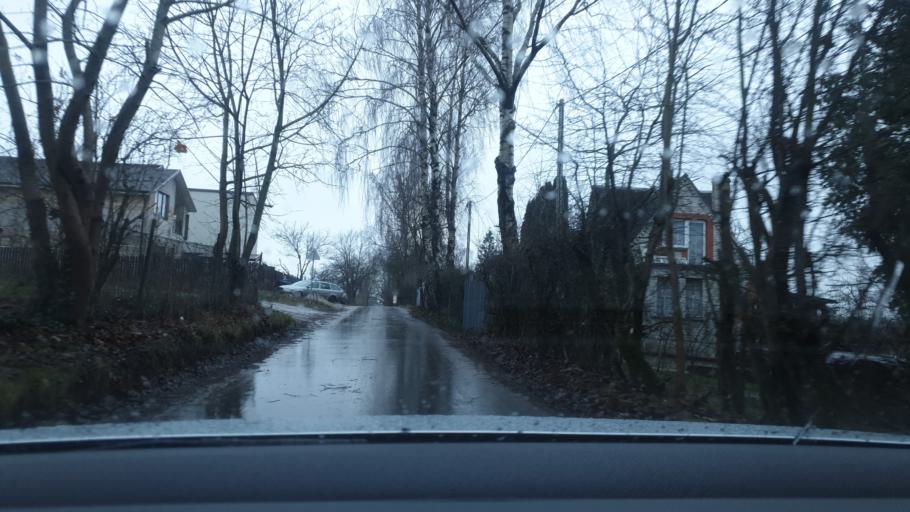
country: LT
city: Skaidiskes
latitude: 54.7057
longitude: 25.4087
